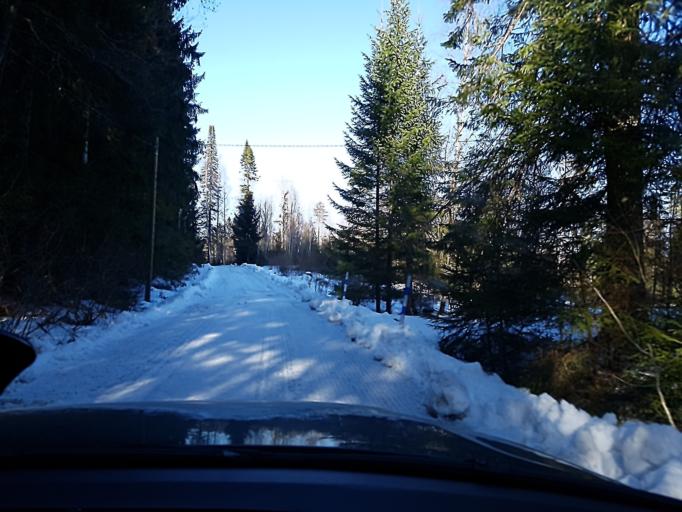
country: FI
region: Uusimaa
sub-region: Helsinki
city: Karjalohja
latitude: 60.2089
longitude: 23.7054
